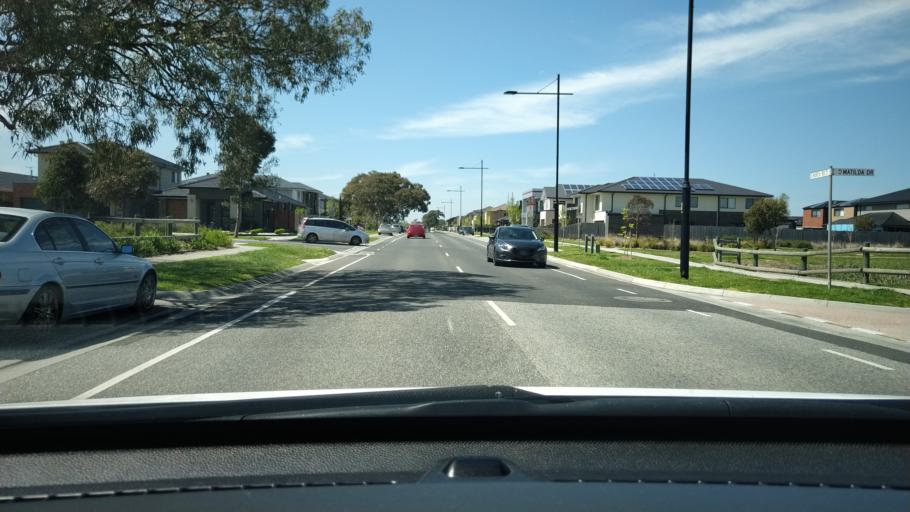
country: AU
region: Victoria
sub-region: Greater Dandenong
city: Keysborough
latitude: -38.0007
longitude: 145.1646
